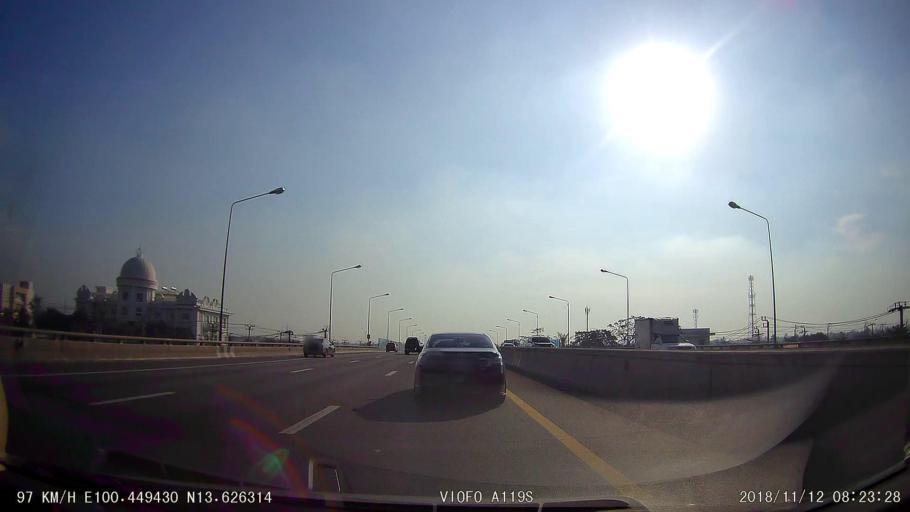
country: TH
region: Bangkok
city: Bang Khun Thian
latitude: 13.6263
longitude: 100.4514
